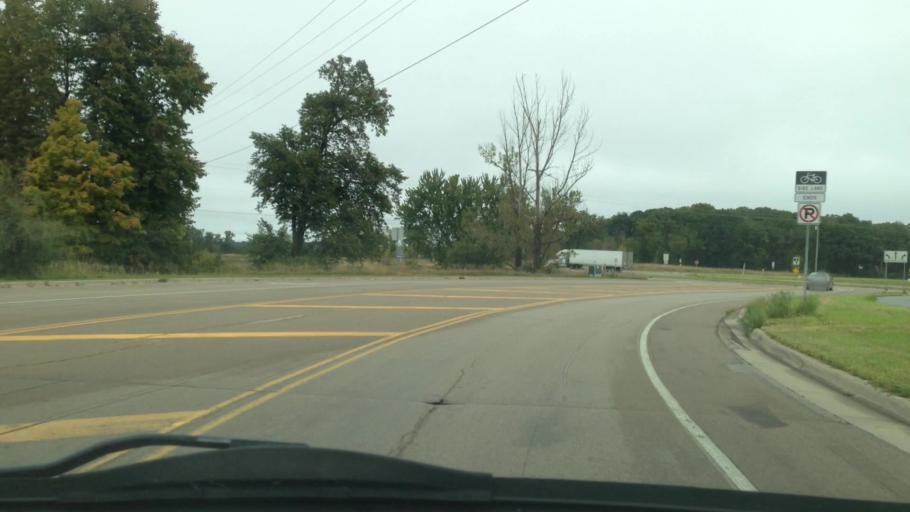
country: US
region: Minnesota
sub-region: Olmsted County
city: Oronoco
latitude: 44.0925
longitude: -92.5085
